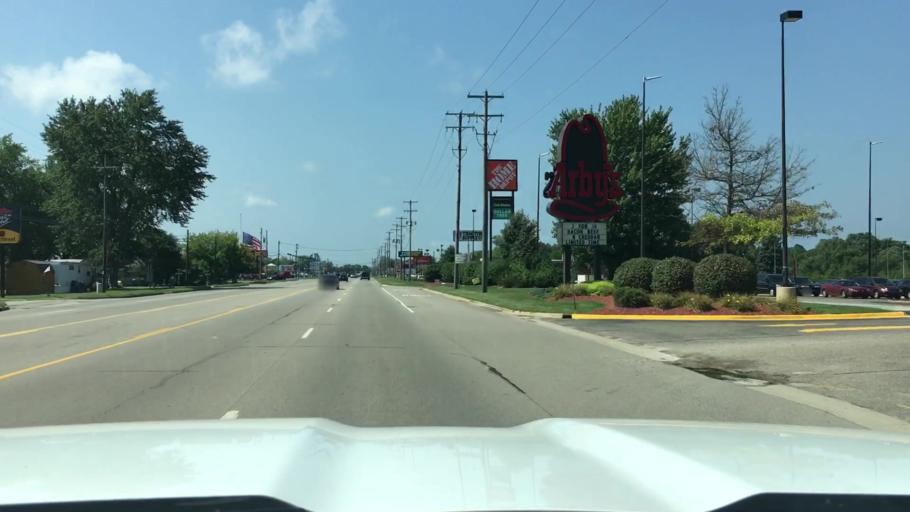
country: US
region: Michigan
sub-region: Allegan County
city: Plainwell
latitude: 42.4500
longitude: -85.6628
